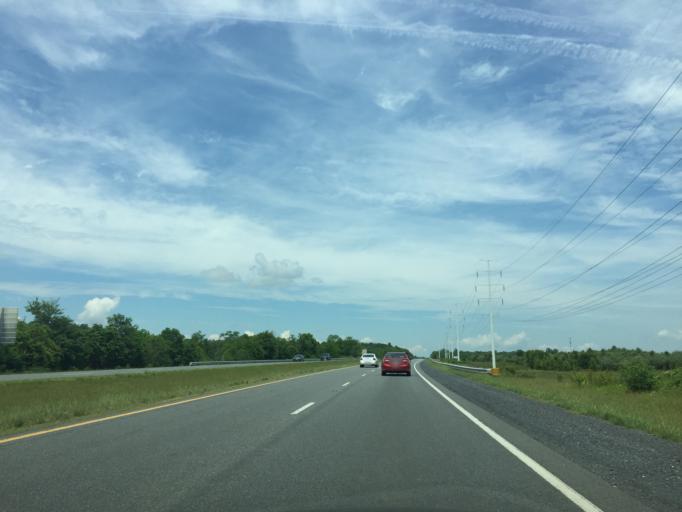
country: US
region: Virginia
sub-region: Frederick County
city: Stephens City
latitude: 39.1360
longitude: -78.2088
